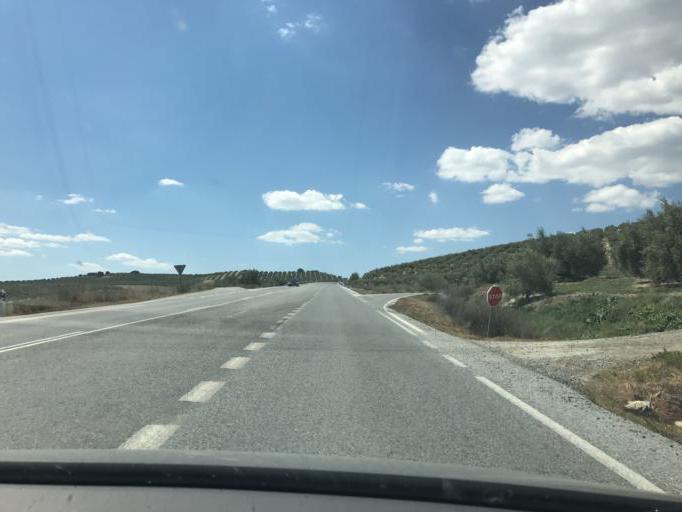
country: ES
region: Andalusia
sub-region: Provincia de Granada
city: Benalua de las Villas
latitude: 37.4279
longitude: -3.7441
